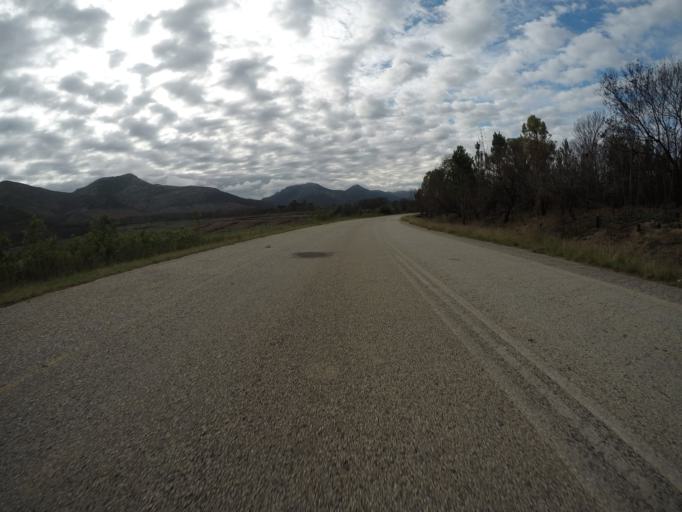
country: ZA
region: Eastern Cape
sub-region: Cacadu District Municipality
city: Kareedouw
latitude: -34.0117
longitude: 24.3109
